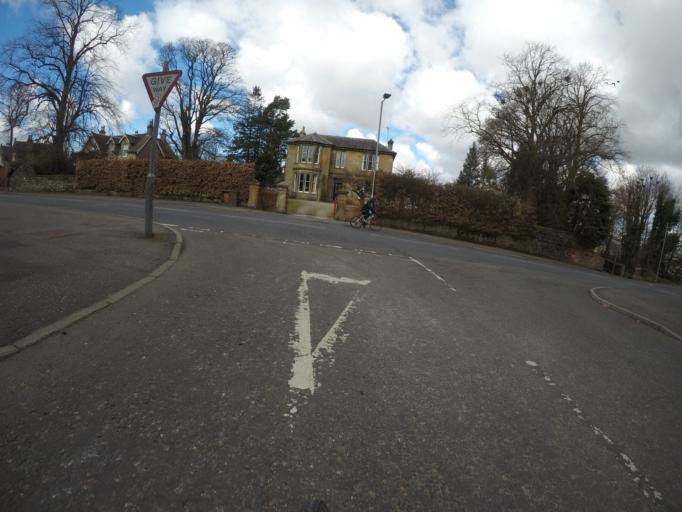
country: GB
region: Scotland
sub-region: North Ayrshire
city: Beith
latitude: 55.7482
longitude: -4.6375
